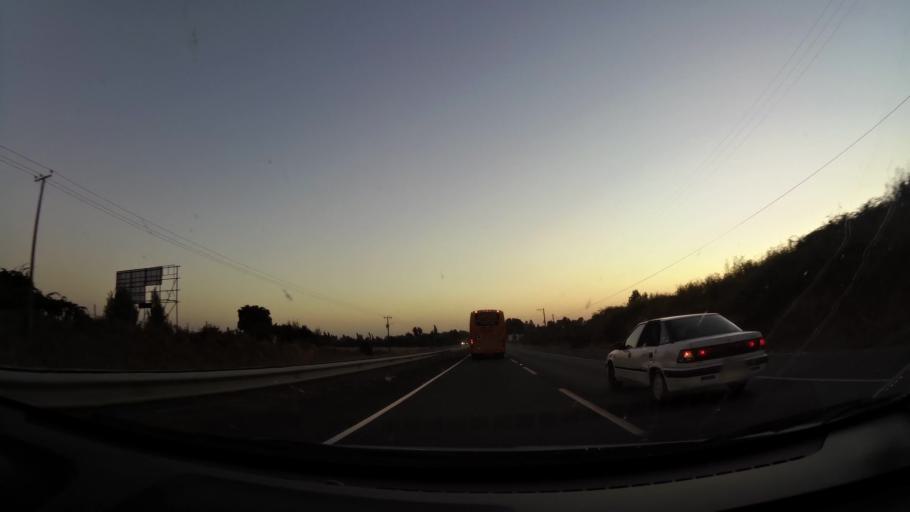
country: CL
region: Maule
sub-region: Provincia de Linares
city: Longavi
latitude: -36.0243
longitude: -71.7455
